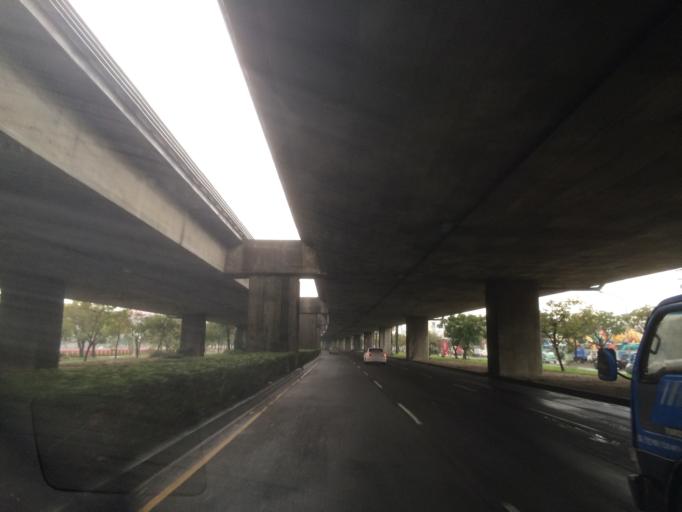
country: TW
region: Taiwan
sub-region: Taichung City
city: Taichung
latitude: 24.1586
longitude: 120.6264
